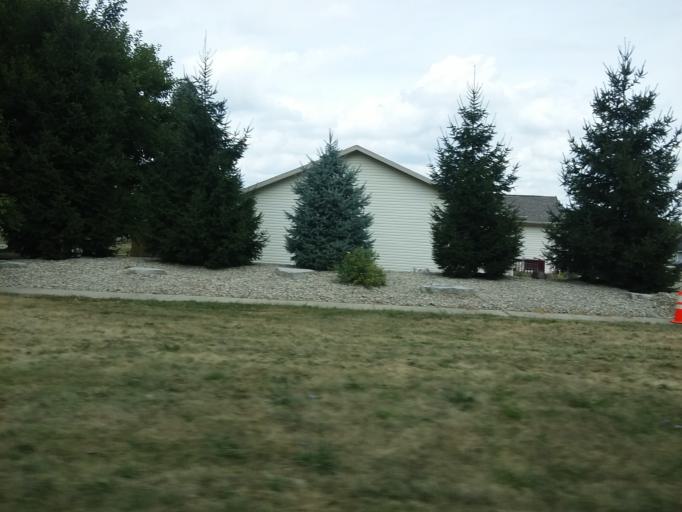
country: US
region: Ohio
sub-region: Hancock County
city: Findlay
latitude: 41.0421
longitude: -83.6823
